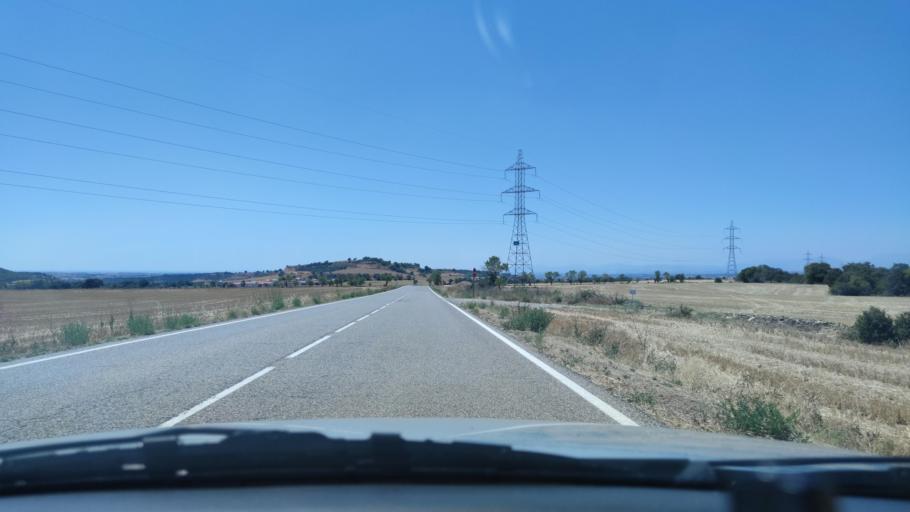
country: ES
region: Catalonia
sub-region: Provincia de Lleida
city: Ivorra
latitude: 41.7268
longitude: 1.3517
